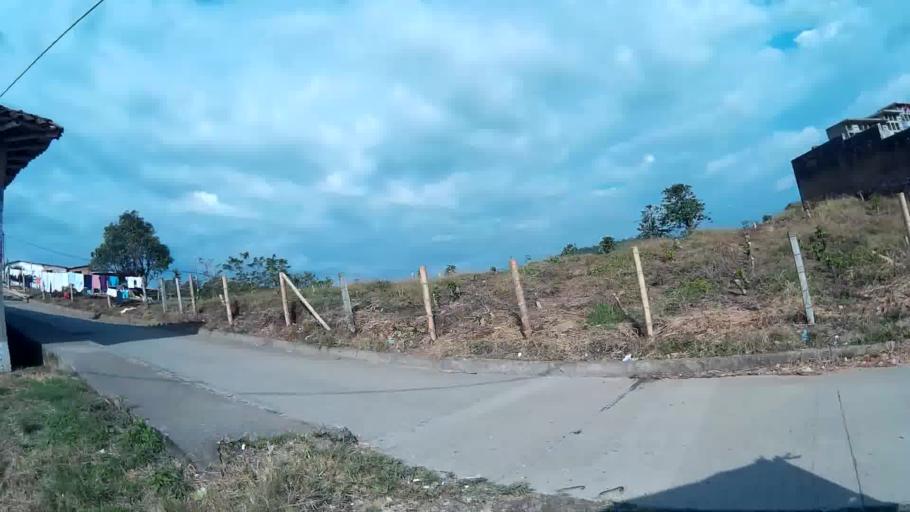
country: CO
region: Valle del Cauca
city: Ulloa
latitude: 4.7168
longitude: -75.7175
